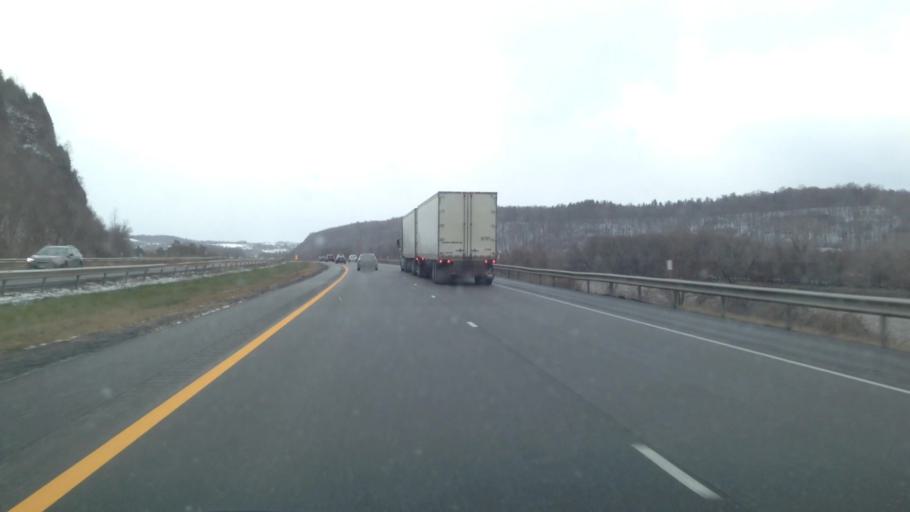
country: US
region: New York
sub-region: Montgomery County
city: Canajoharie
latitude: 42.8959
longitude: -74.4793
